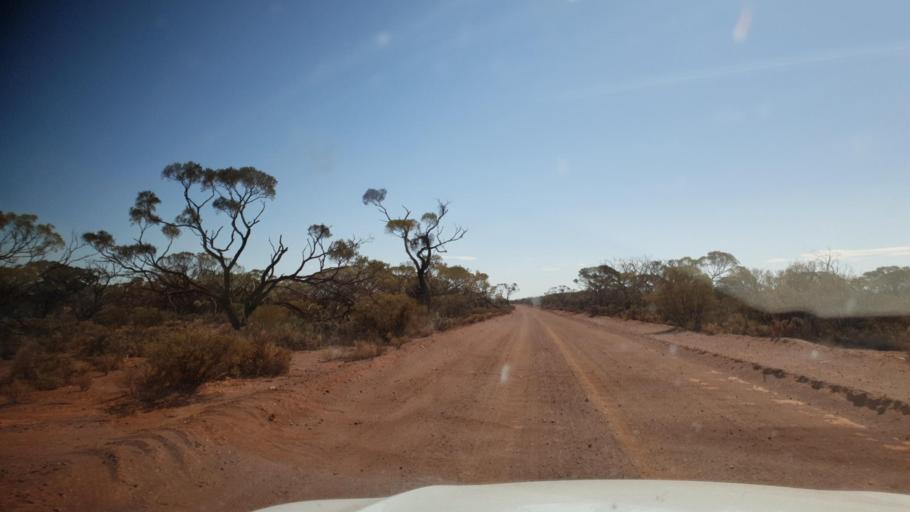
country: AU
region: South Australia
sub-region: Kimba
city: Caralue
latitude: -32.5213
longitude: 136.1370
